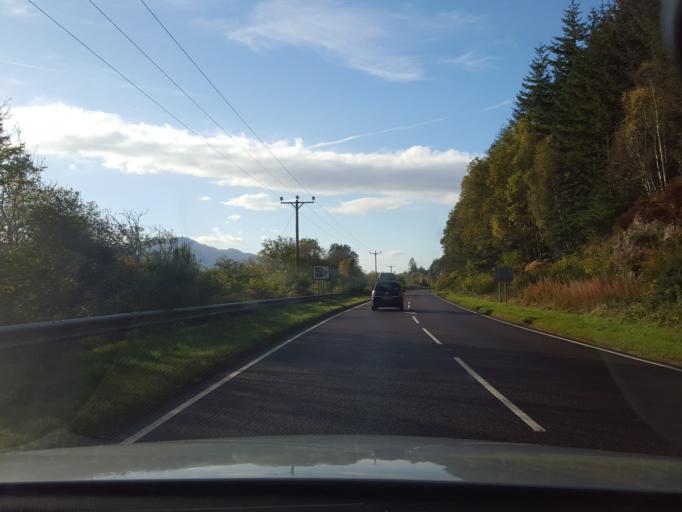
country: GB
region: Scotland
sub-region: Highland
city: Beauly
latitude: 57.2320
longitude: -4.5638
